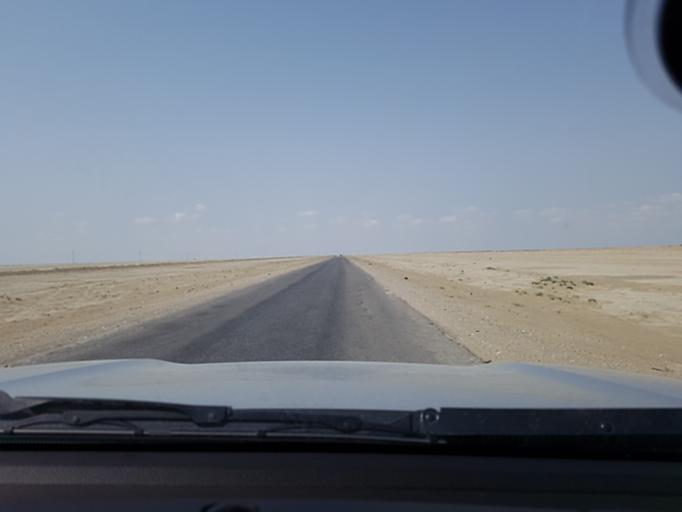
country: TM
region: Balkan
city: Gumdag
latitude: 38.6741
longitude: 54.4089
